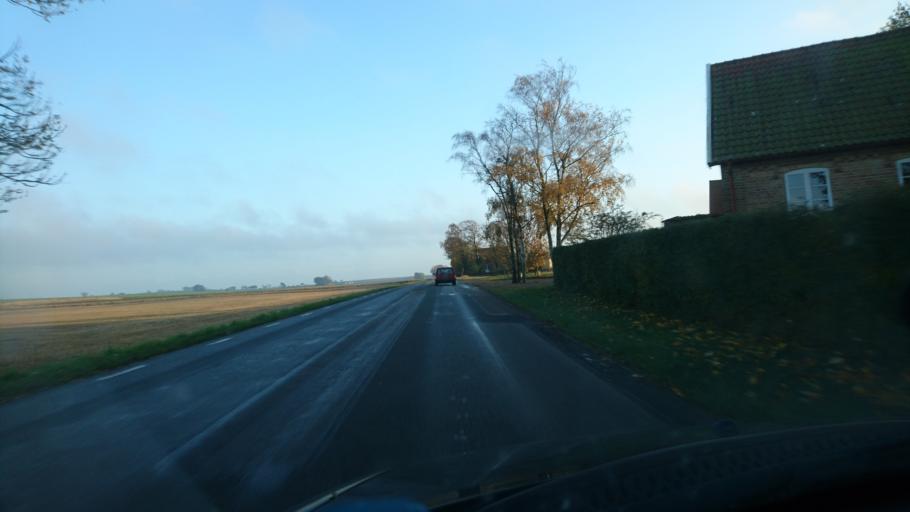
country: SE
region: Skane
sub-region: Ystads Kommun
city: Kopingebro
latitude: 55.4586
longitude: 14.1085
